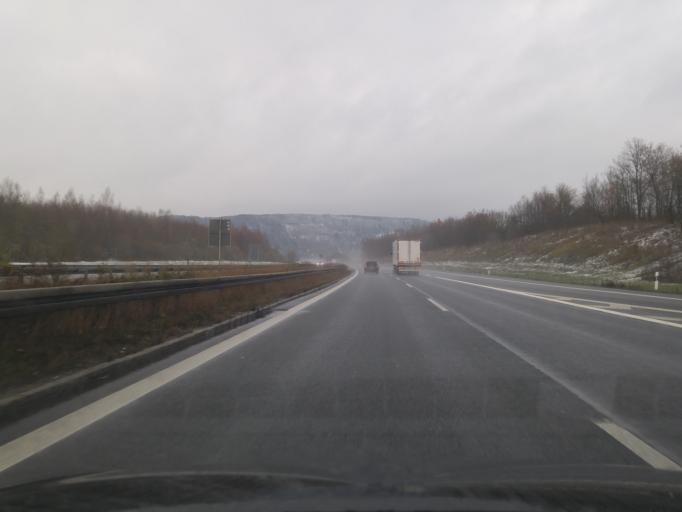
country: DE
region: Bavaria
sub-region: Regierungsbezirk Unterfranken
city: Elfershausen
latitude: 50.1266
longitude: 9.9581
